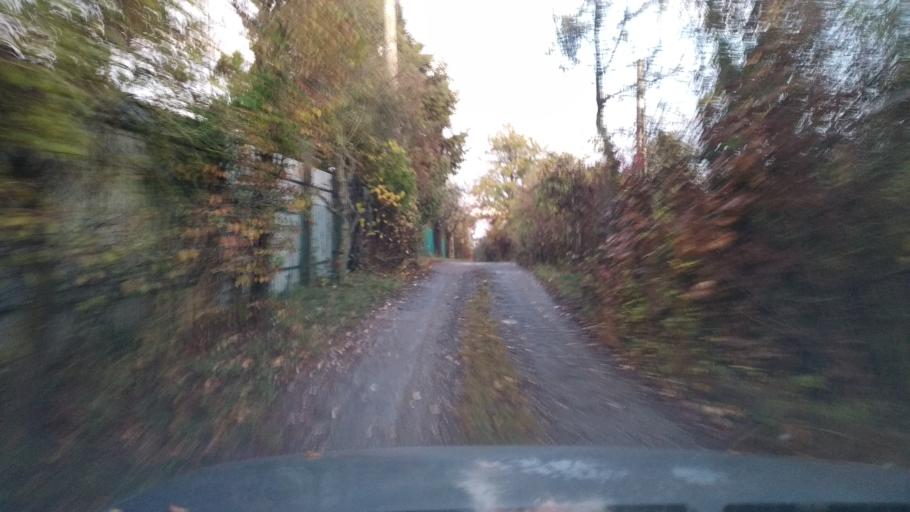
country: HU
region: Pest
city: Nagykovacsi
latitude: 47.6642
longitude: 19.0015
